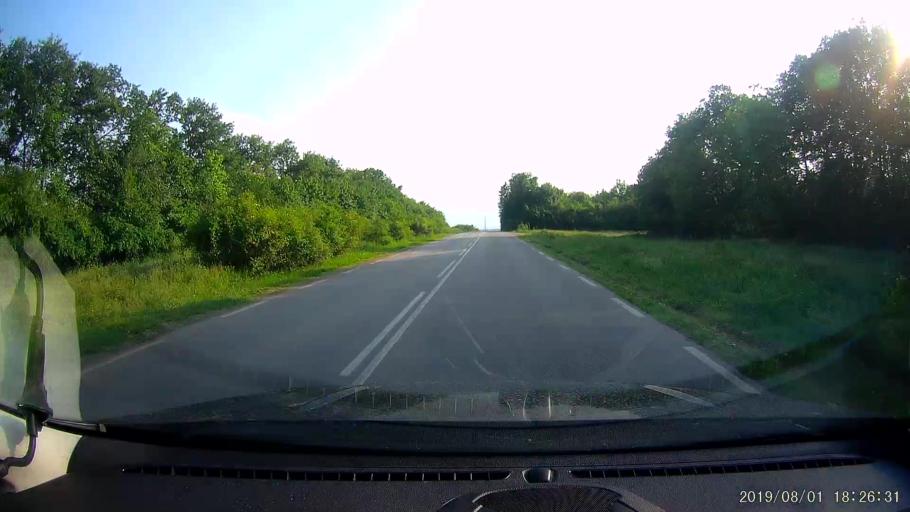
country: BG
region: Shumen
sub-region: Obshtina Venets
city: Venets
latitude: 43.5996
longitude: 26.9909
